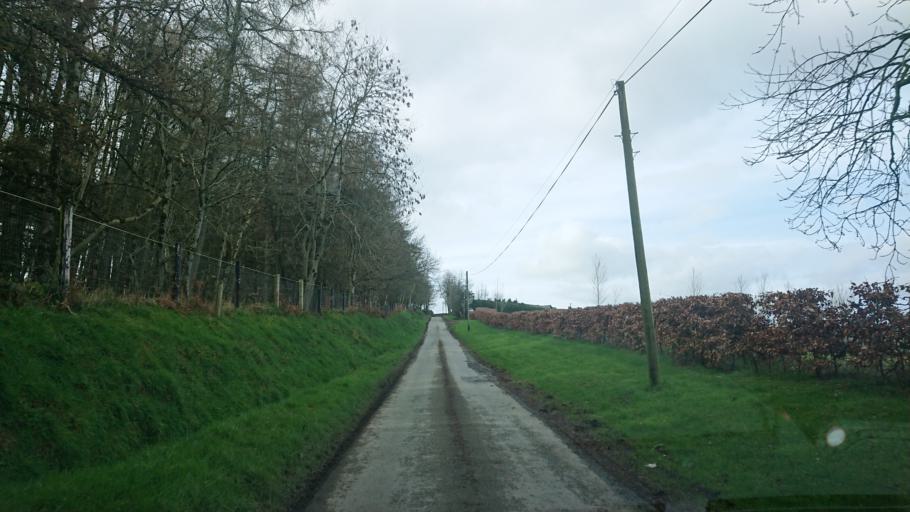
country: IE
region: Leinster
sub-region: Wicklow
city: Blessington
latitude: 53.1550
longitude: -6.5687
